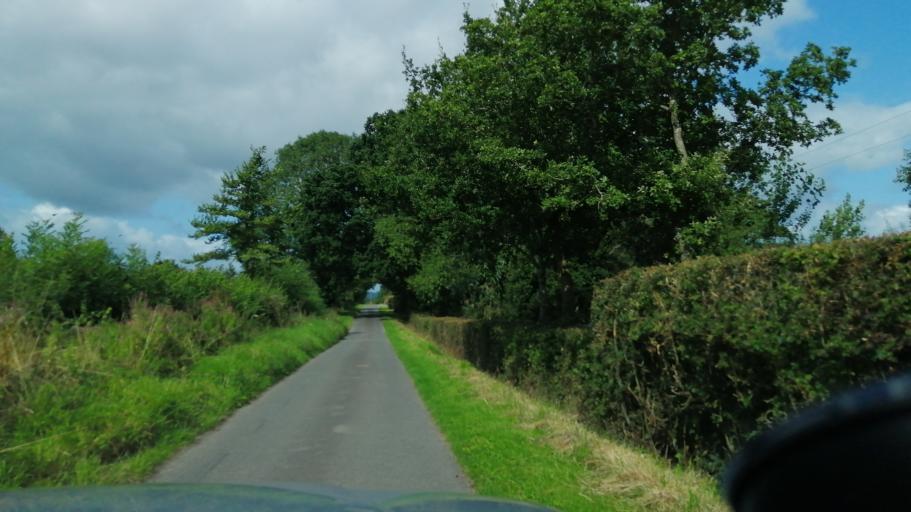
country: GB
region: England
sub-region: Herefordshire
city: Kinnersley
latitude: 52.1314
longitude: -2.9333
